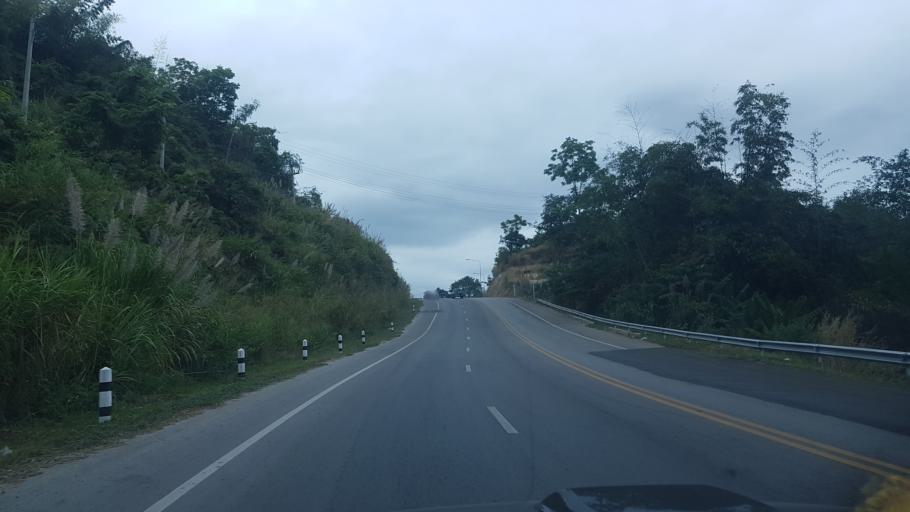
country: TH
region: Phetchabun
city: Khao Kho
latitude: 16.5559
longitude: 101.0267
